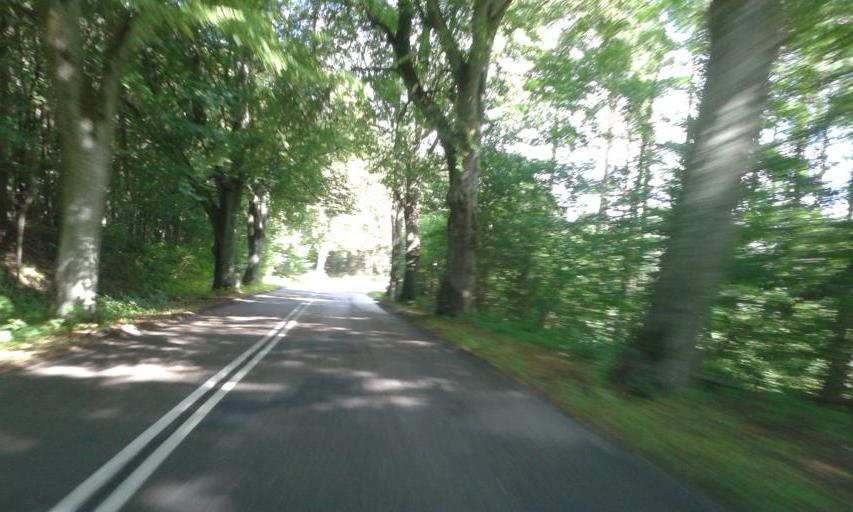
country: PL
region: West Pomeranian Voivodeship
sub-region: Powiat koszalinski
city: Bobolice
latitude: 53.9954
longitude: 16.7003
